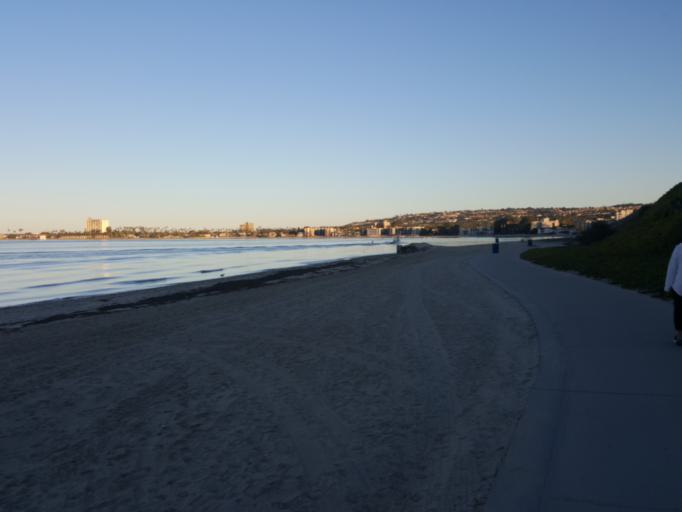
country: US
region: California
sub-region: San Diego County
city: La Jolla
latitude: 32.7825
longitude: -117.2394
